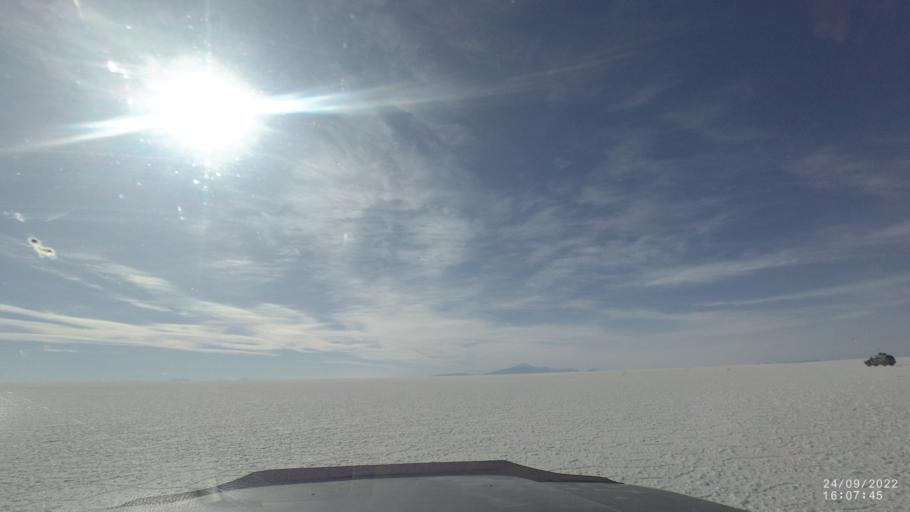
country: BO
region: Potosi
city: Colchani
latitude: -20.2976
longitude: -67.3052
